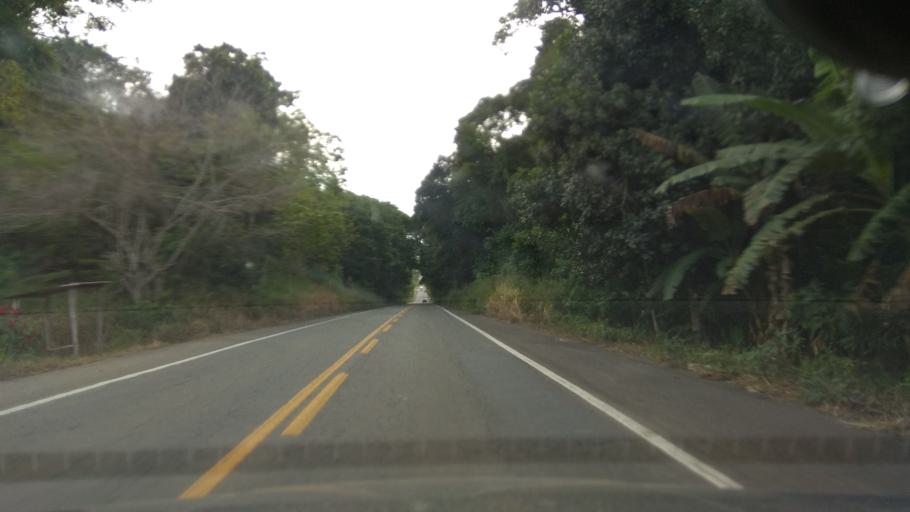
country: BR
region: Bahia
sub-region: Ubaitaba
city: Ubaitaba
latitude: -14.2625
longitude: -39.3399
